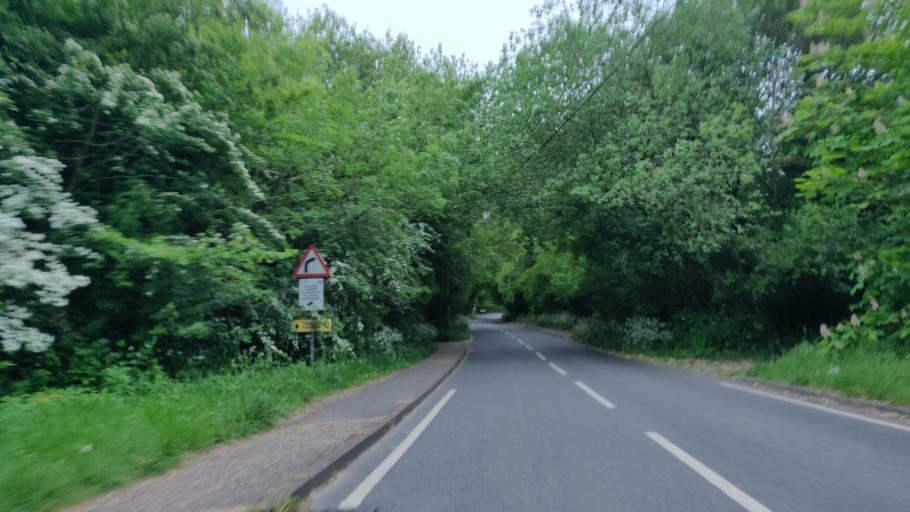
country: GB
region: England
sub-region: West Sussex
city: Southwater
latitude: 51.0358
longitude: -0.3433
